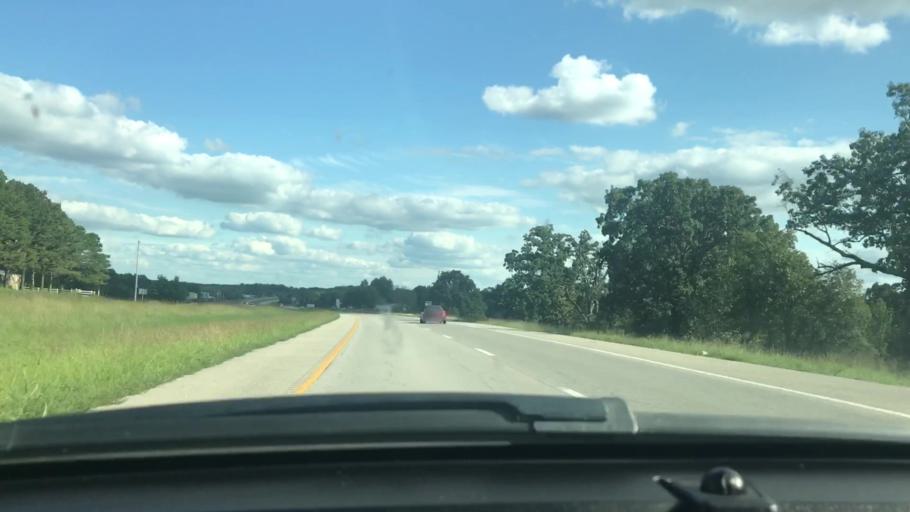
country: US
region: Missouri
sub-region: Howell County
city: West Plains
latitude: 36.8162
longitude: -91.9083
